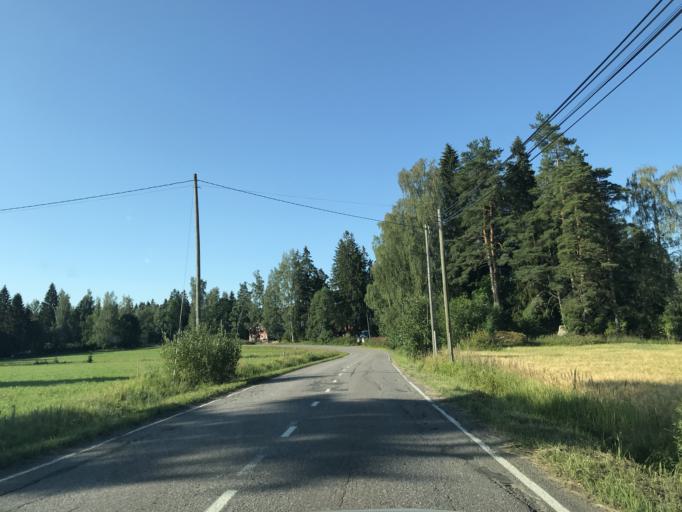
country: FI
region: Uusimaa
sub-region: Helsinki
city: Lohja
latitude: 60.2897
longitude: 24.1384
